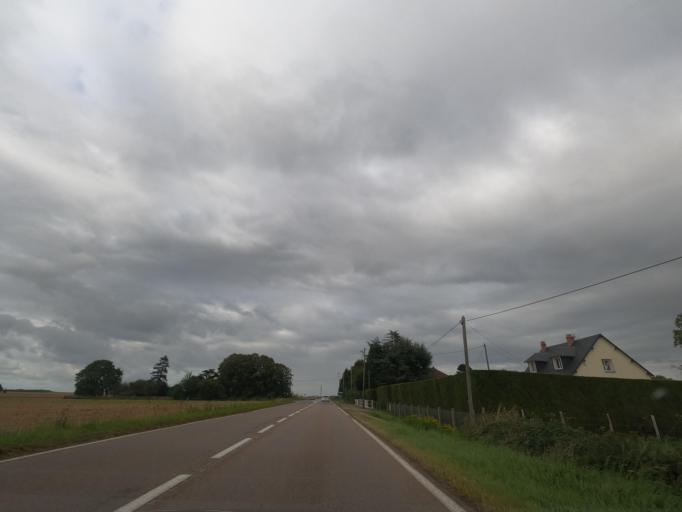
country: FR
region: Haute-Normandie
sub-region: Departement de l'Eure
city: Bourgtheroulde-Infreville
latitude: 49.2859
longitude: 0.8455
